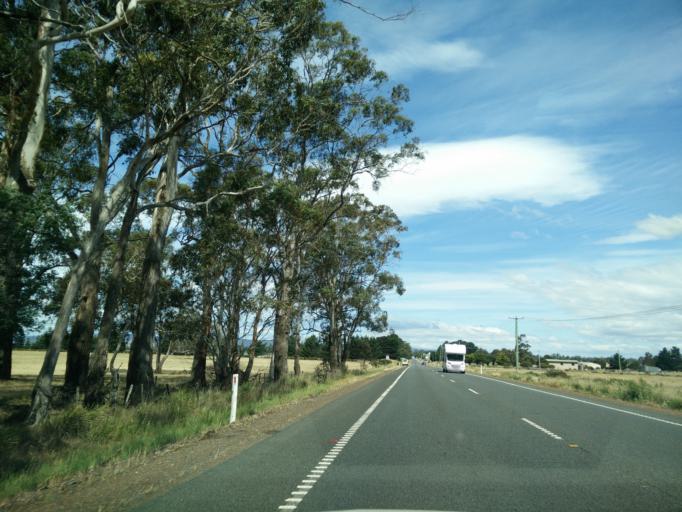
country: AU
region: Tasmania
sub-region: Northern Midlands
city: Evandale
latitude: -41.7995
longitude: 147.3977
